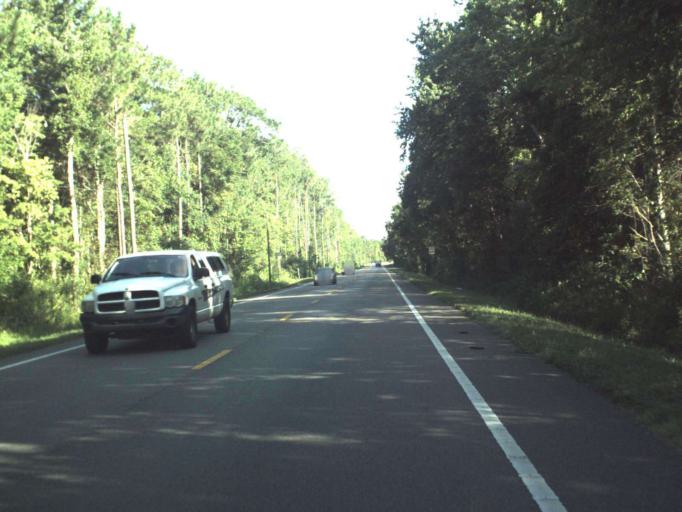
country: US
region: Florida
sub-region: Lake County
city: Four Corners
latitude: 28.3696
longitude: -81.8215
